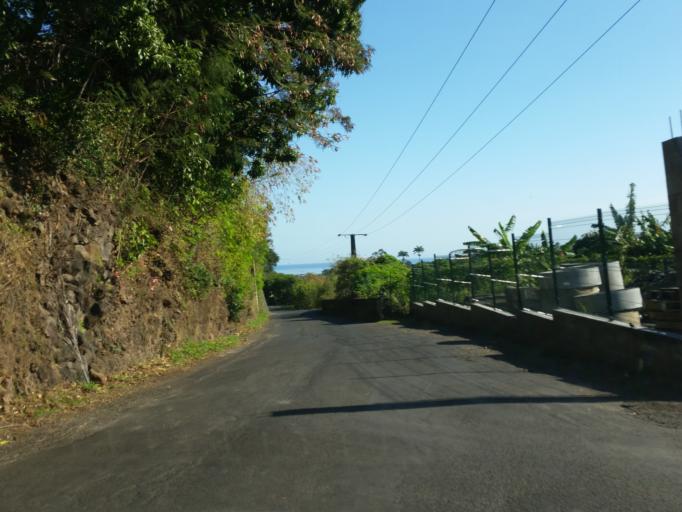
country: RE
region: Reunion
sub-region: Reunion
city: Sainte-Marie
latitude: -20.9185
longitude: 55.5103
